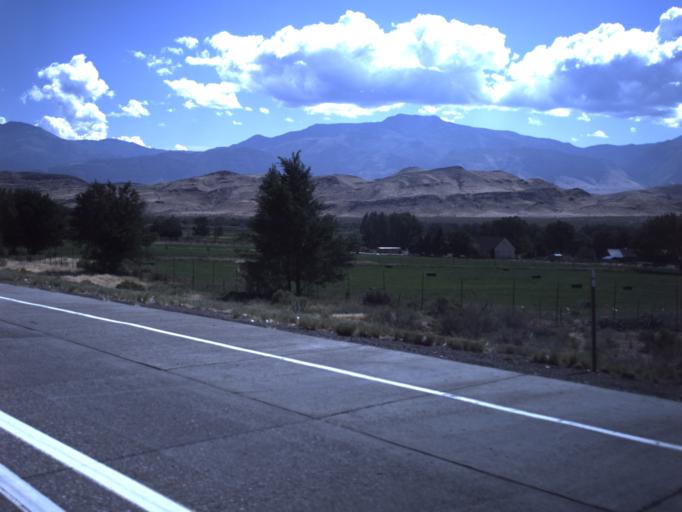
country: US
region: Utah
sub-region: Sevier County
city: Monroe
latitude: 38.6011
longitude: -112.2482
